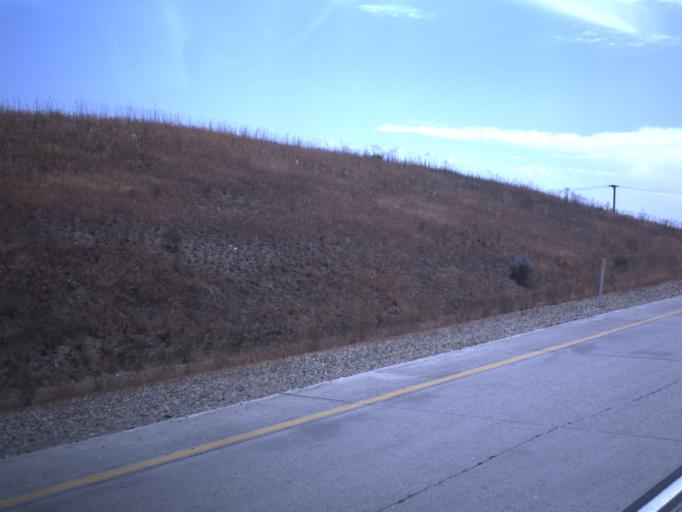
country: US
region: Utah
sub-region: Salt Lake County
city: Oquirrh
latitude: 40.6405
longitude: -112.0462
